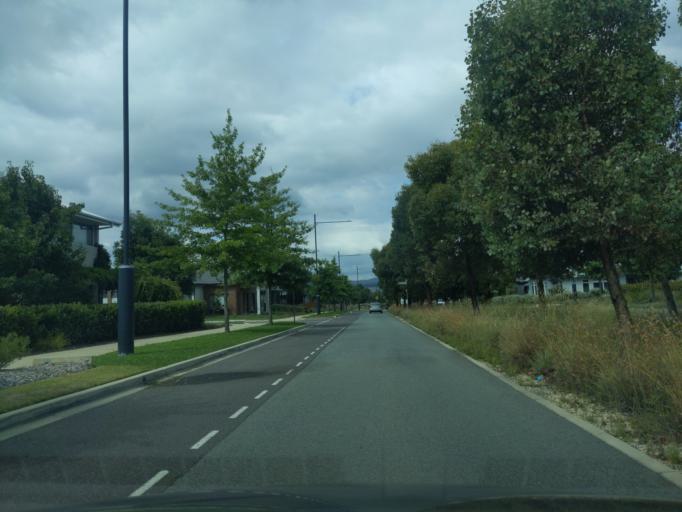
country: AU
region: New South Wales
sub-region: Queanbeyan
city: Queanbeyan
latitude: -35.4176
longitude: 149.2307
